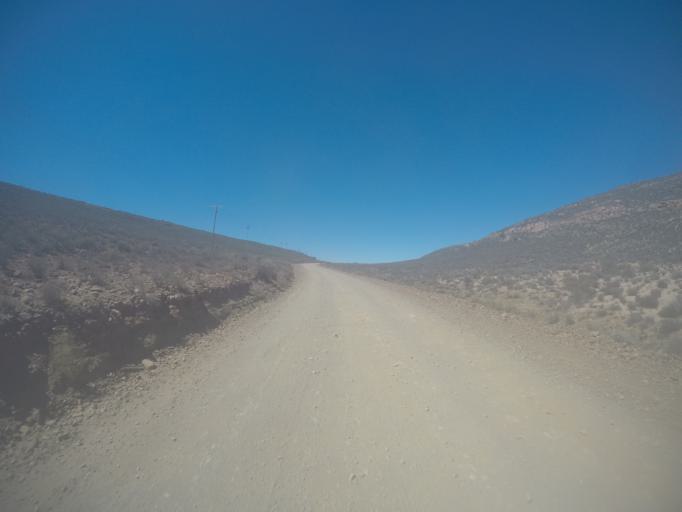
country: ZA
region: Western Cape
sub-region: West Coast District Municipality
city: Clanwilliam
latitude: -32.5275
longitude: 19.3530
